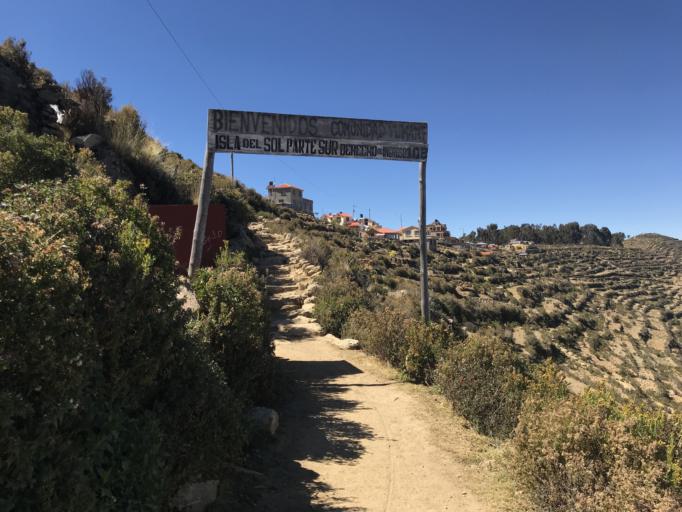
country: BO
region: La Paz
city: Yumani
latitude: -16.0343
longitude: -69.1527
